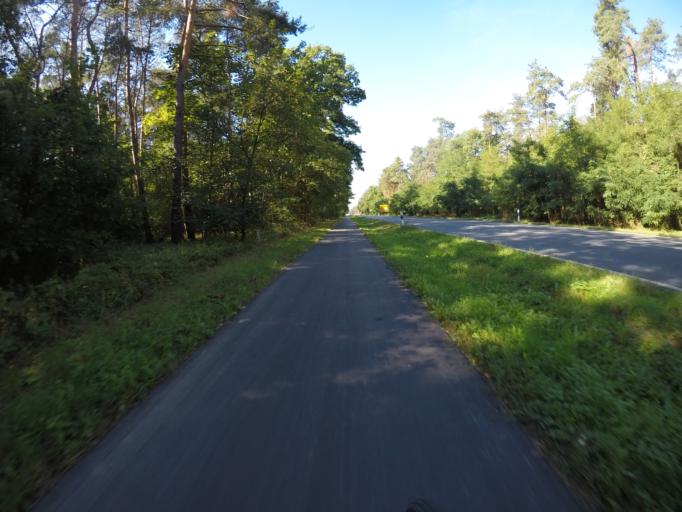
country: DE
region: Hesse
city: Pfungstadt
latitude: 49.8304
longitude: 8.5842
